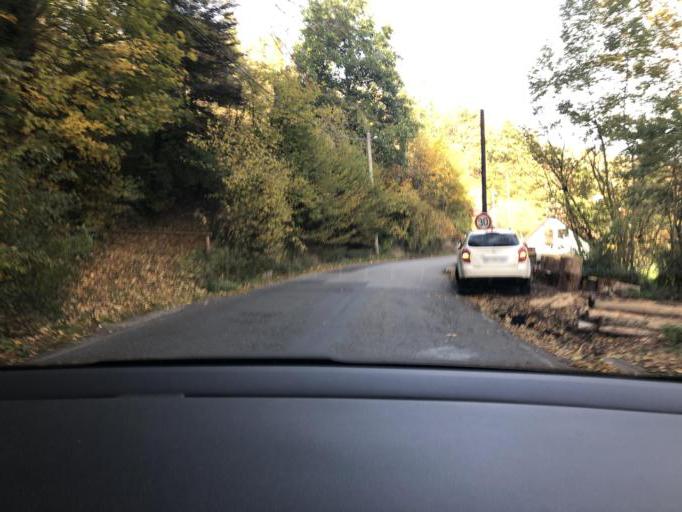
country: CZ
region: Central Bohemia
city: Divisov
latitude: 49.8093
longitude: 14.9252
